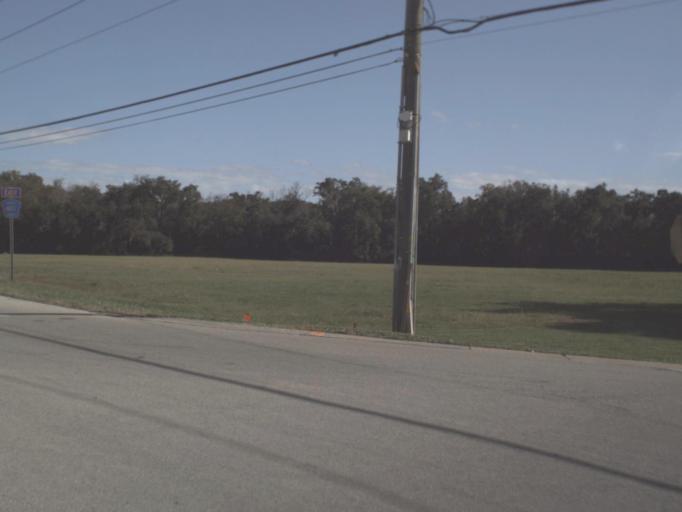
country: US
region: Florida
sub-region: Volusia County
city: Samsula-Spruce Creek
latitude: 29.0843
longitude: -81.0574
